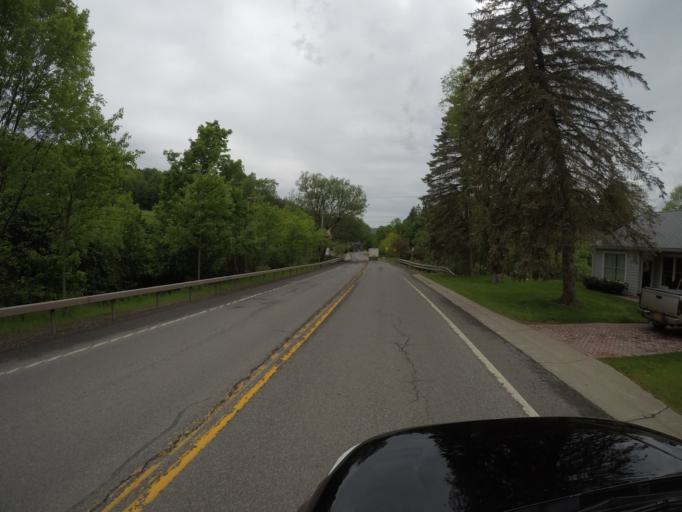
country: US
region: New York
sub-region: Delaware County
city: Delhi
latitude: 42.1929
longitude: -74.7739
